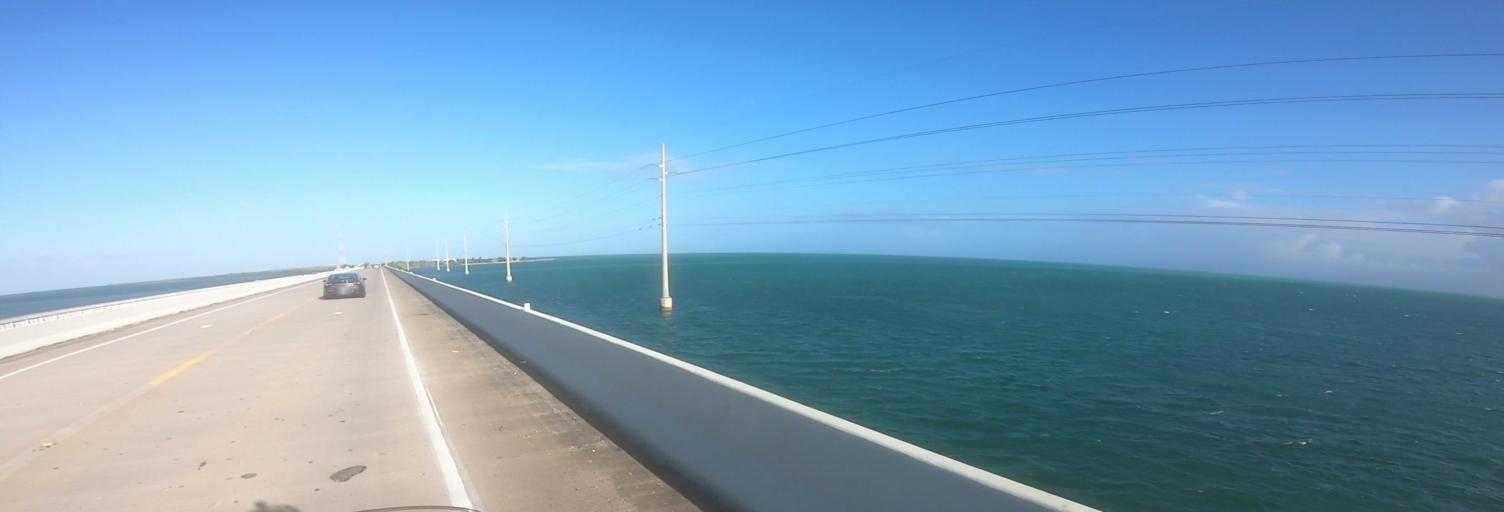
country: US
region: Florida
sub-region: Monroe County
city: Big Pine Key
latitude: 24.6473
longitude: -81.3233
